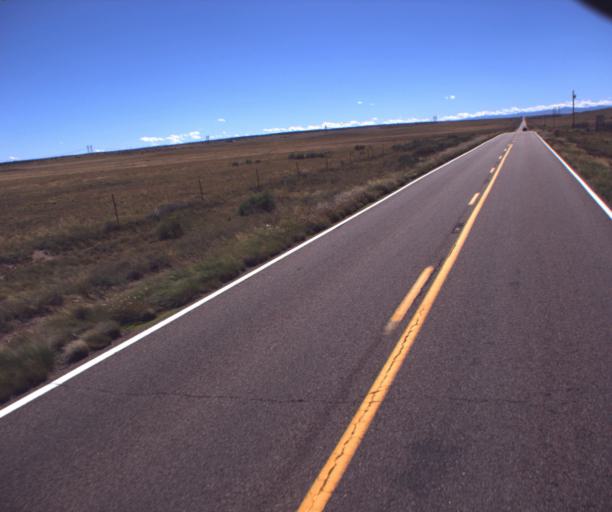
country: US
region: Arizona
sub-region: Apache County
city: Saint Johns
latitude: 34.5983
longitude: -109.3256
